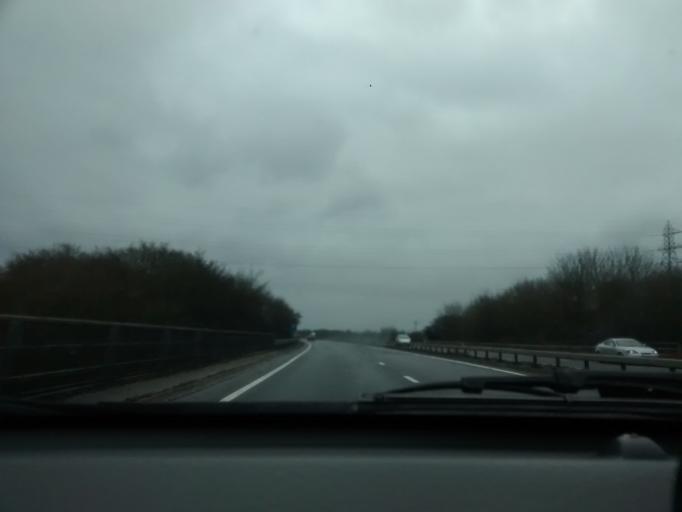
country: GB
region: England
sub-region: Suffolk
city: Stowmarket
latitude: 52.1868
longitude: 1.0229
